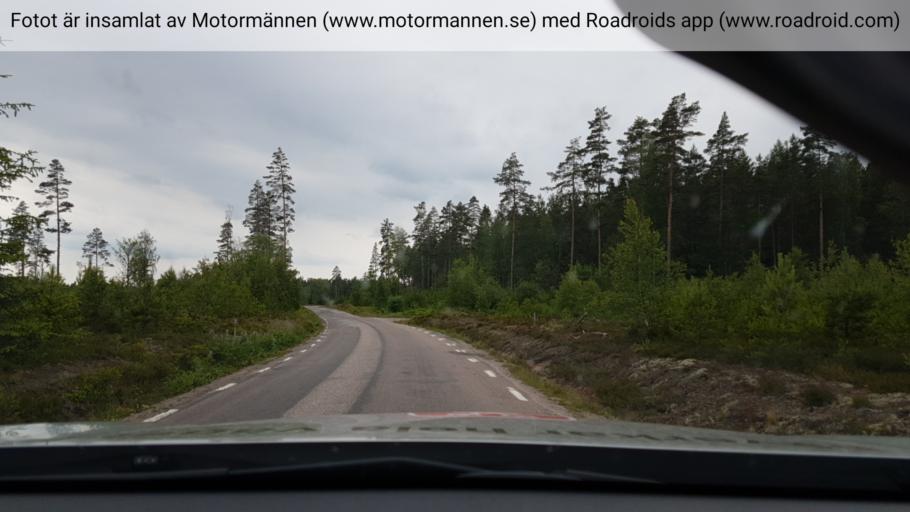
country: SE
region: Vaestra Goetaland
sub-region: Tidaholms Kommun
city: Tidaholm
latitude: 58.0604
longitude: 14.0479
